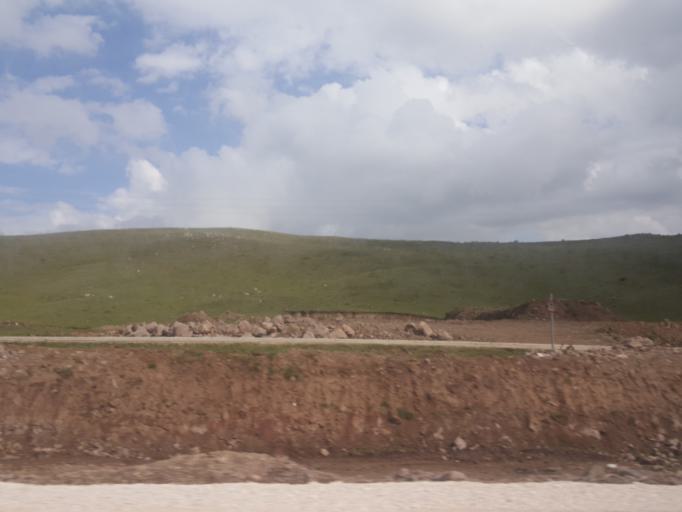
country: TR
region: Tokat
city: Bereketli
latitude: 40.5643
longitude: 37.3042
